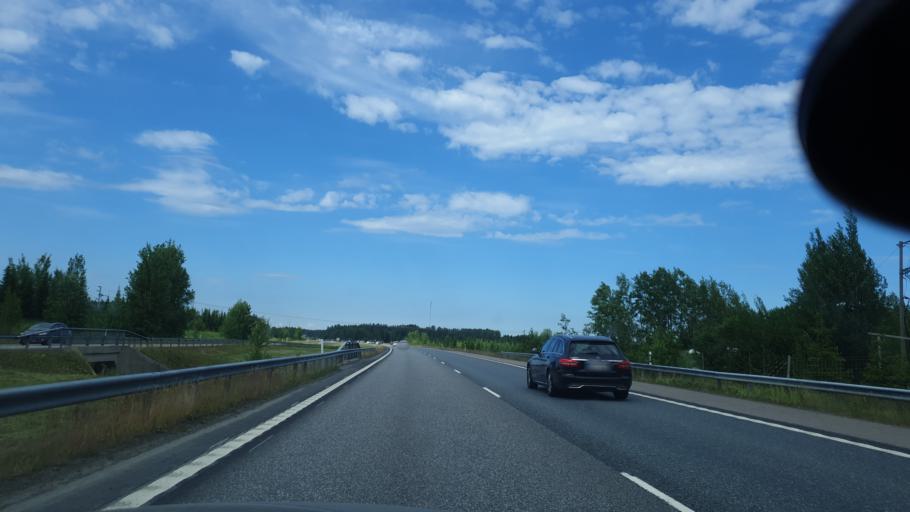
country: FI
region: Uusimaa
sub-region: Helsinki
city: Jaervenpaeae
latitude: 60.5304
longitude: 25.1668
